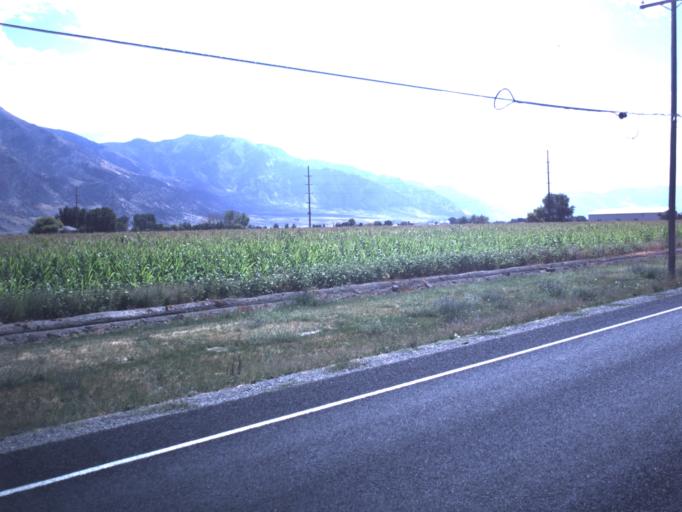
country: US
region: Utah
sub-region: Box Elder County
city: Garland
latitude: 41.7291
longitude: -112.1430
